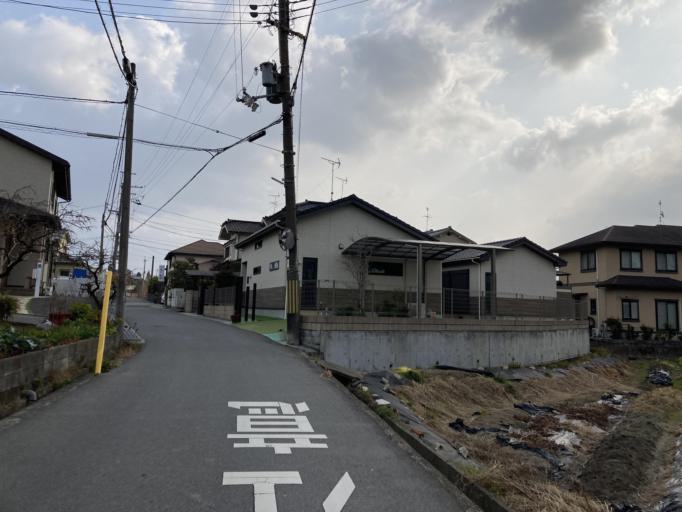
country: JP
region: Nara
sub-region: Ikoma-shi
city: Ikoma
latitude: 34.6095
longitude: 135.7162
